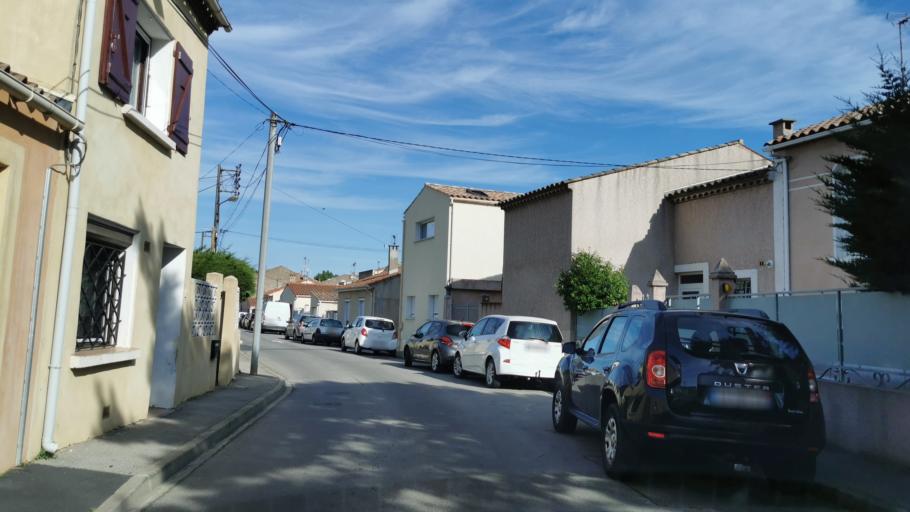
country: FR
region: Languedoc-Roussillon
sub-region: Departement de l'Aude
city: Narbonne
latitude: 43.1809
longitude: 2.9939
